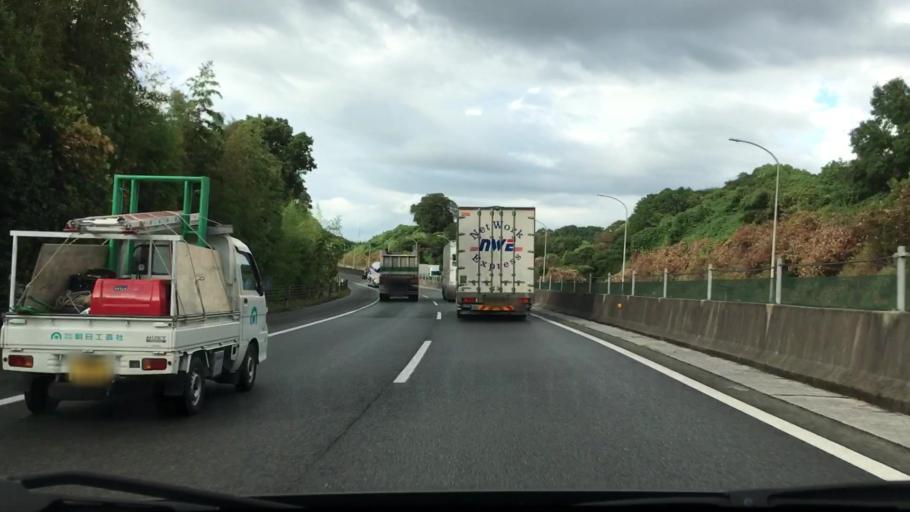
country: JP
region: Fukuoka
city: Nishifukuma
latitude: 33.7440
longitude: 130.5257
